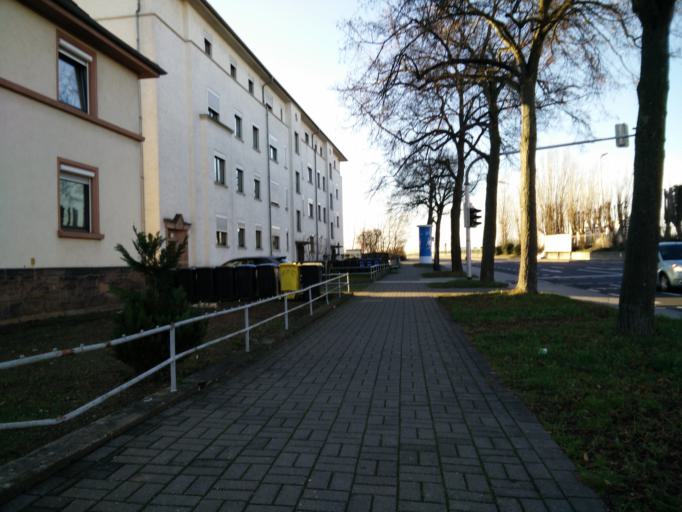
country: DE
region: Hesse
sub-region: Regierungsbezirk Kassel
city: Fulda
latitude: 50.5461
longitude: 9.6918
